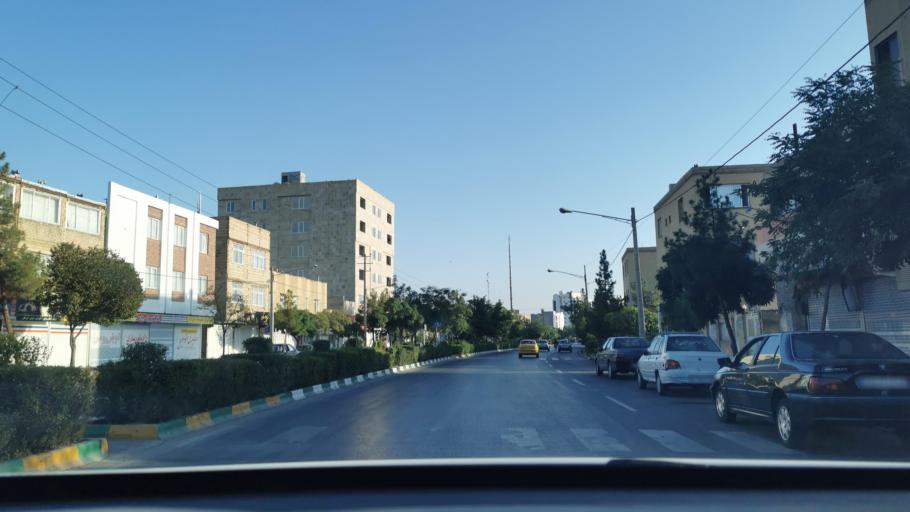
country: IR
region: Razavi Khorasan
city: Mashhad
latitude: 36.3551
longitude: 59.5130
